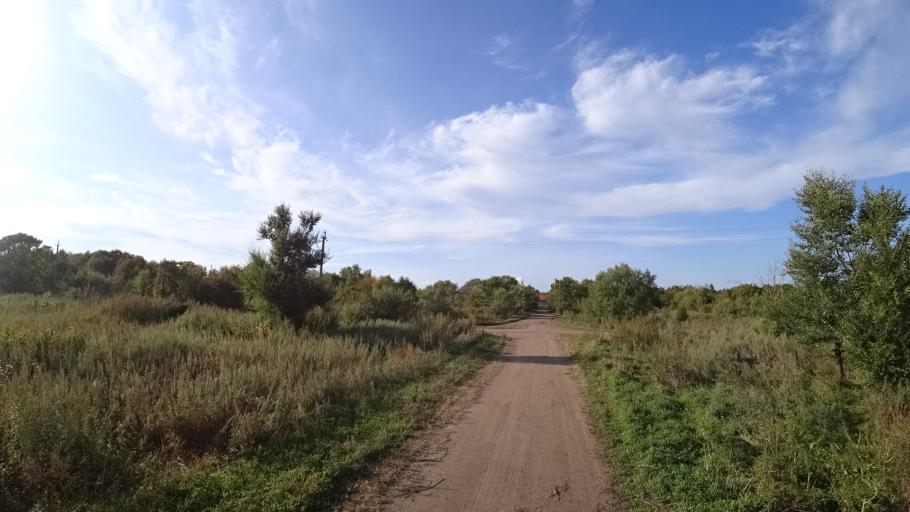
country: RU
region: Amur
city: Arkhara
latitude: 49.3502
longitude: 130.1059
